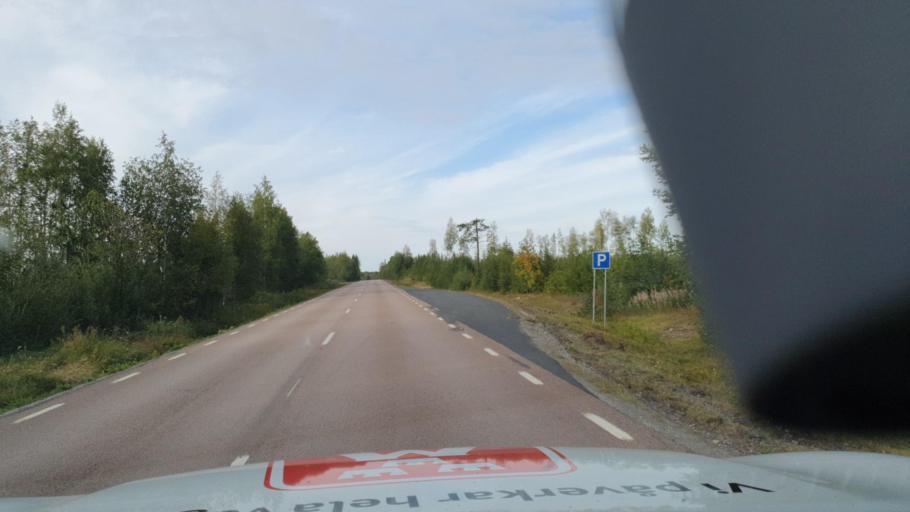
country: SE
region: Jaemtland
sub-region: Stroemsunds Kommun
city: Stroemsund
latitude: 63.7676
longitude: 15.7084
